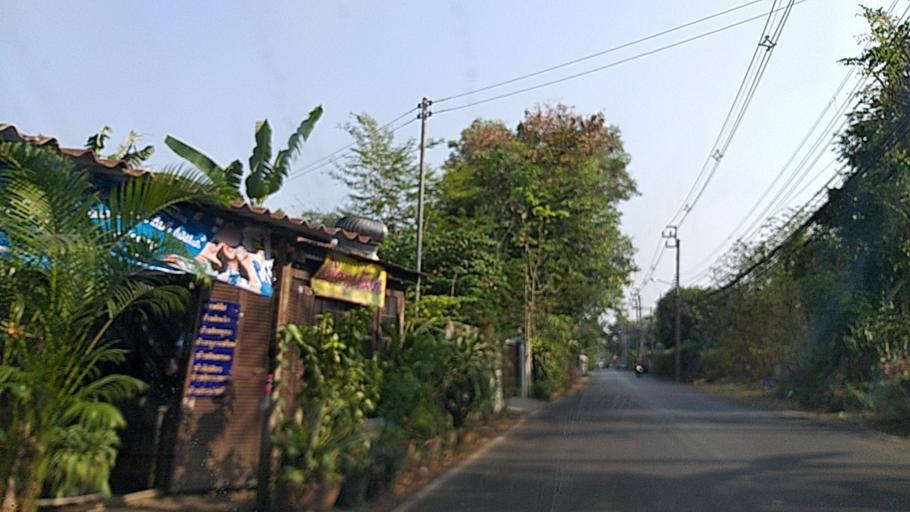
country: TH
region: Bangkok
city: Don Mueang
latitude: 13.9347
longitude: 100.5536
